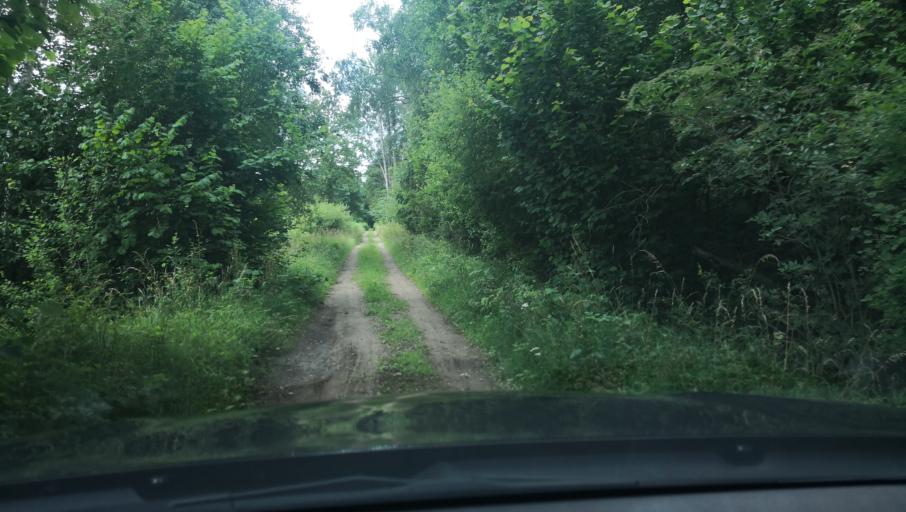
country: SE
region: Skane
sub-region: Simrishamns Kommun
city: Kivik
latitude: 55.6197
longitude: 14.1109
